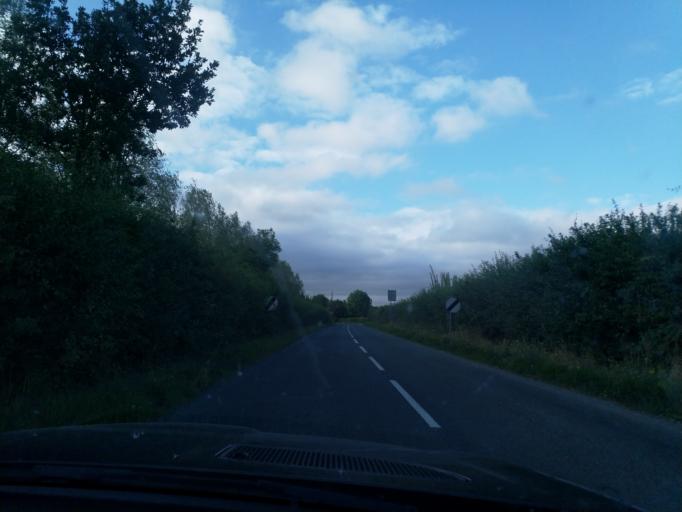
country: GB
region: England
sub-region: Suffolk
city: Stowmarket
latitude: 52.2349
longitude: 0.9707
